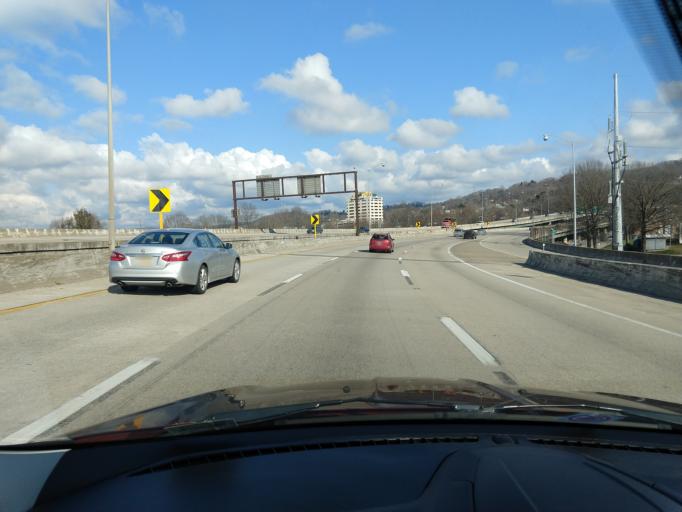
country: US
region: West Virginia
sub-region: Kanawha County
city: Charleston
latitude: 38.3548
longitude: -81.6297
